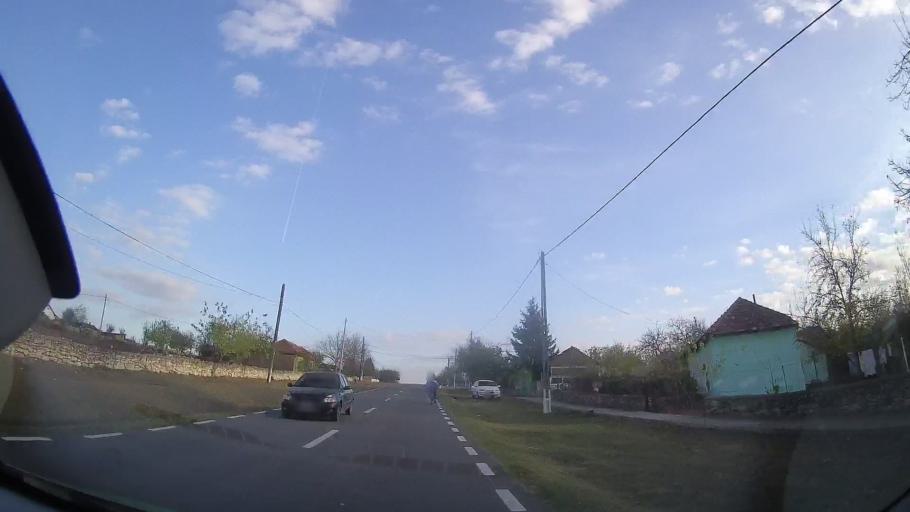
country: RO
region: Constanta
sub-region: Comuna Chirnogeni
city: Plopeni
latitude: 43.9597
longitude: 28.1448
